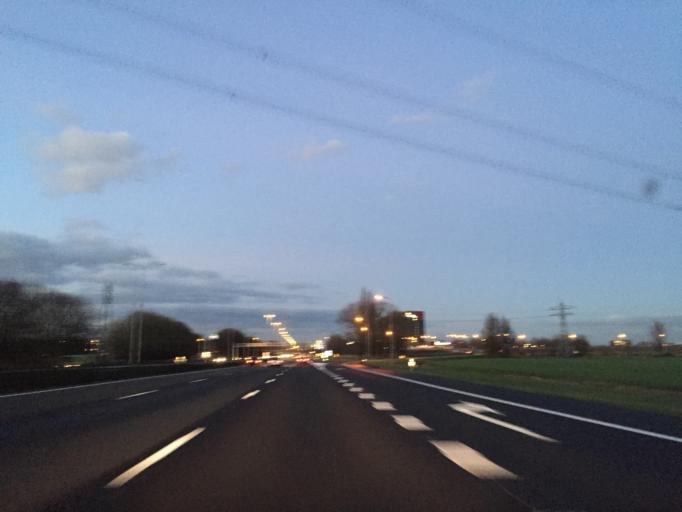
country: NL
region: South Holland
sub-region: Gemeente Dordrecht
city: Dordrecht
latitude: 51.7674
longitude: 4.6480
